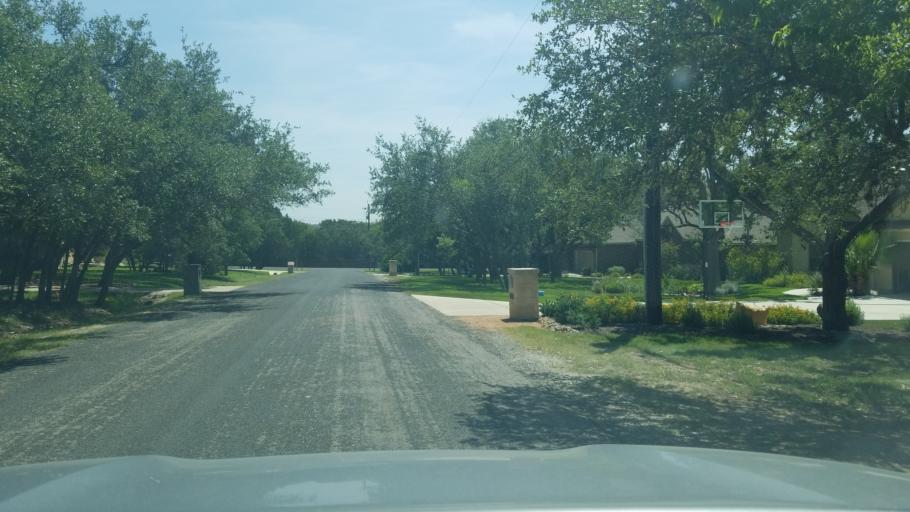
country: US
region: Texas
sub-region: Bexar County
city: Timberwood Park
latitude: 29.7009
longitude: -98.4873
